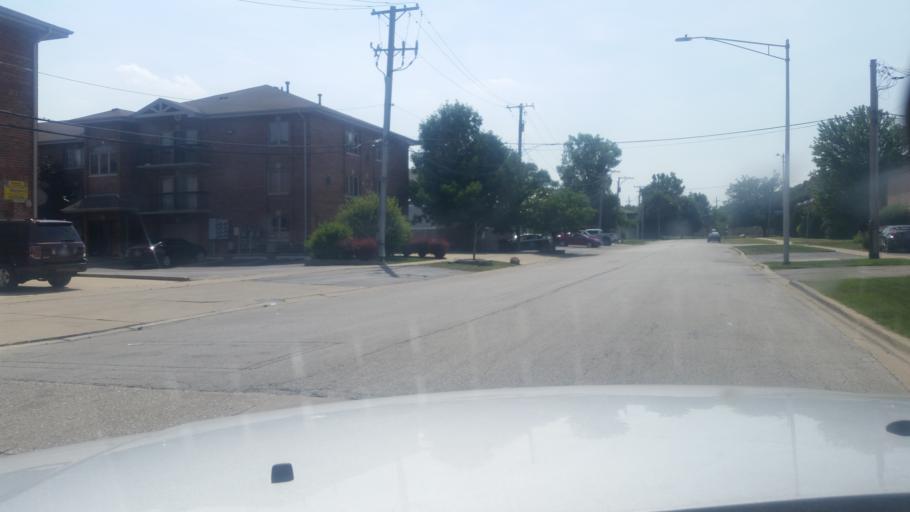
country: US
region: Illinois
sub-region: Cook County
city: Oak Lawn
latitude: 41.6979
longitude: -87.7598
